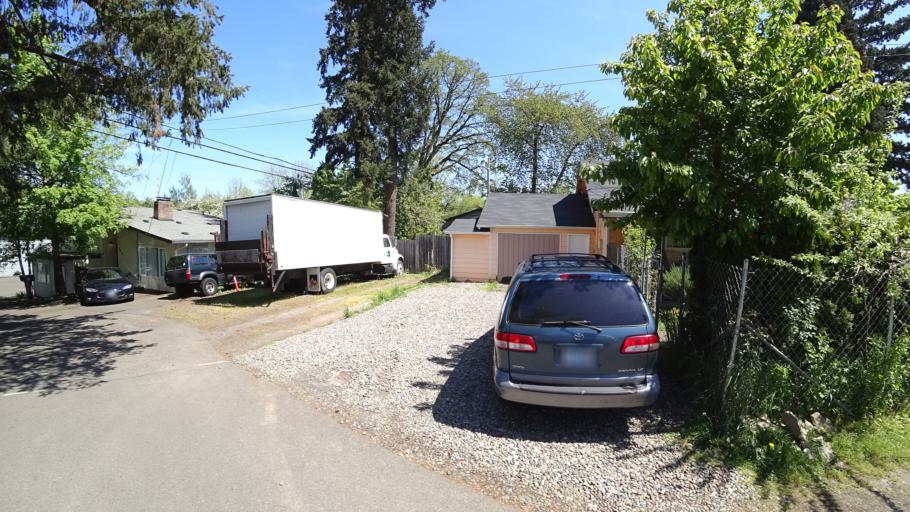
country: US
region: Oregon
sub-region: Washington County
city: Hillsboro
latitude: 45.5198
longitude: -122.9670
